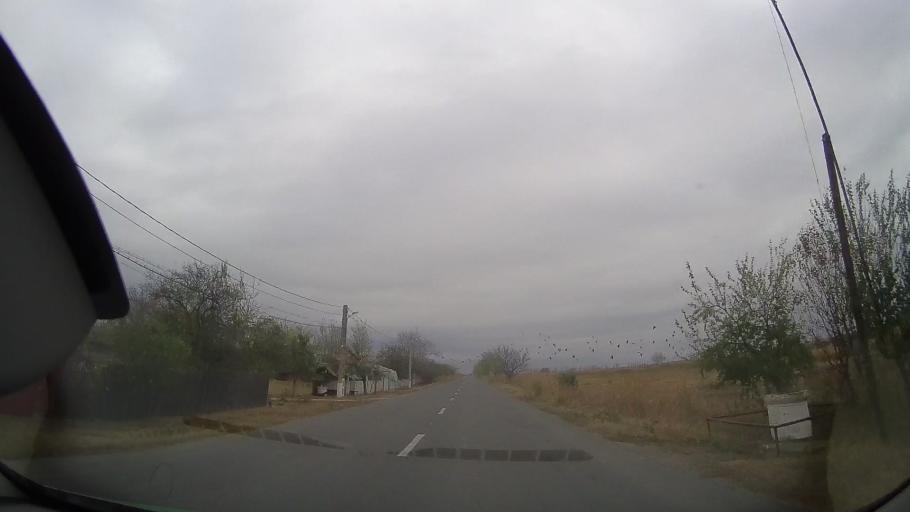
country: RO
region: Ialomita
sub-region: Comuna Milosesti
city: Milosesti
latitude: 44.7555
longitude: 27.2104
